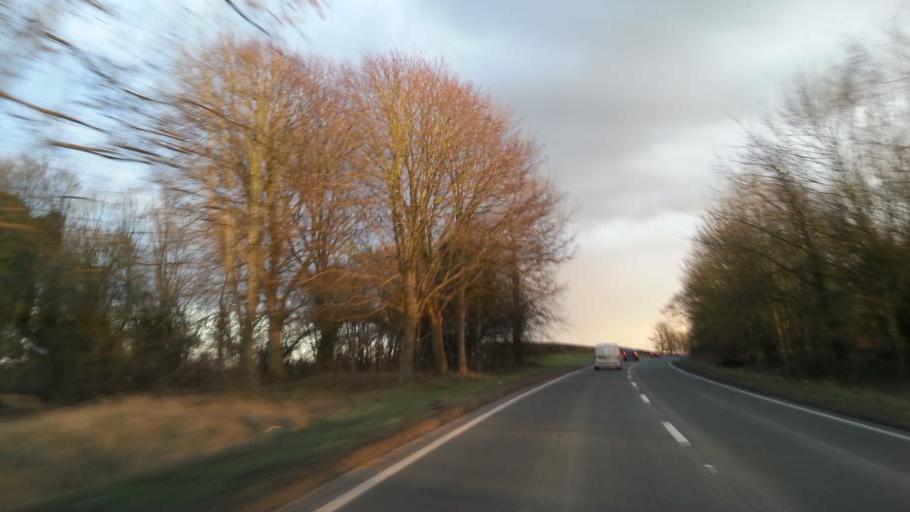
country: GB
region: England
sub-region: Nottinghamshire
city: Farndon
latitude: 53.1183
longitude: -0.8666
